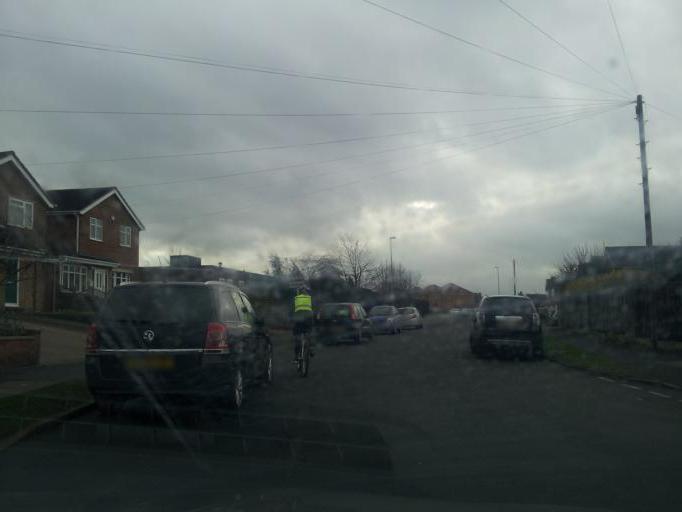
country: GB
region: England
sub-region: Northamptonshire
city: Kettering
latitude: 52.3949
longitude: -0.6985
